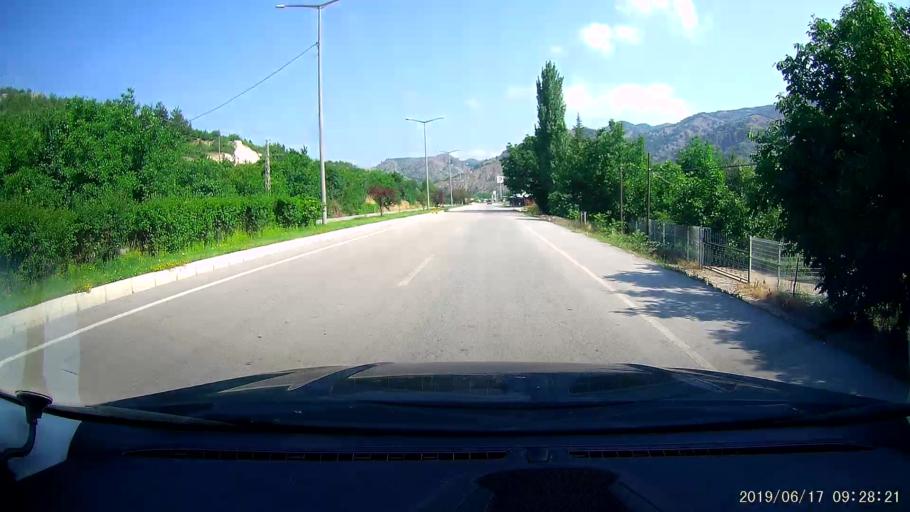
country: TR
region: Amasya
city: Amasya
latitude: 40.6874
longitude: 35.8225
